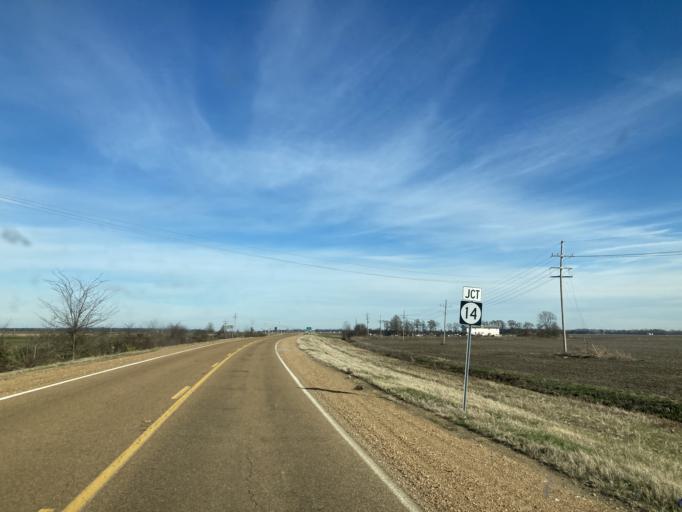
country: US
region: Mississippi
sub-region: Humphreys County
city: Belzoni
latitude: 32.9929
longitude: -90.5888
